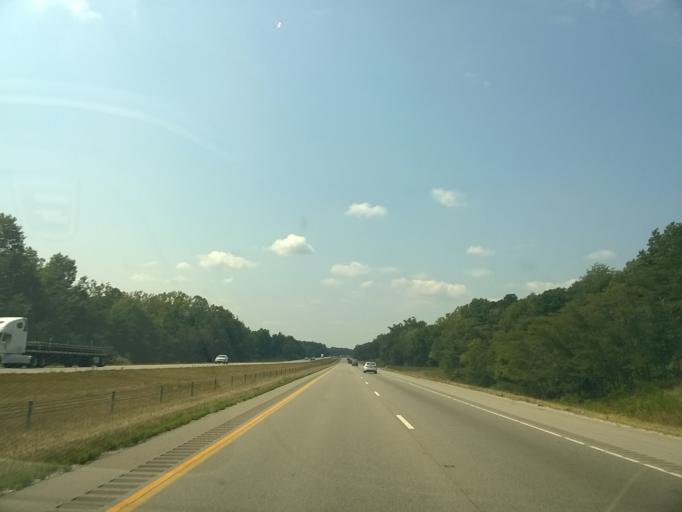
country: US
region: Indiana
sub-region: Clay County
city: Brazil
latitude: 39.4510
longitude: -87.1819
